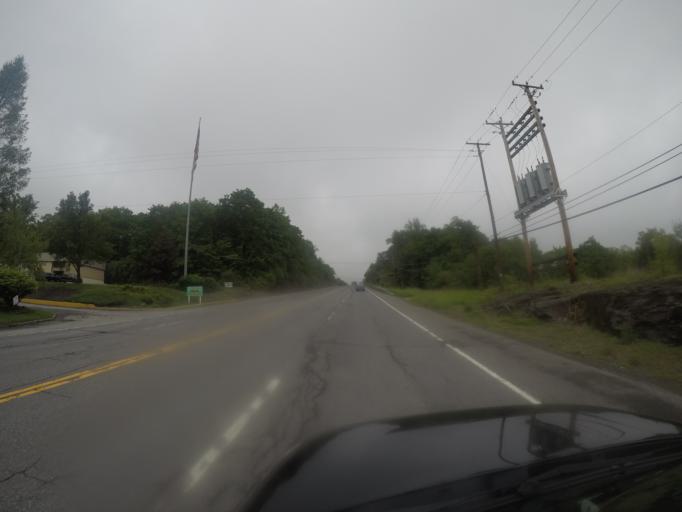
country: US
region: New York
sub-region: Ulster County
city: West Hurley
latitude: 41.9860
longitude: -74.0861
